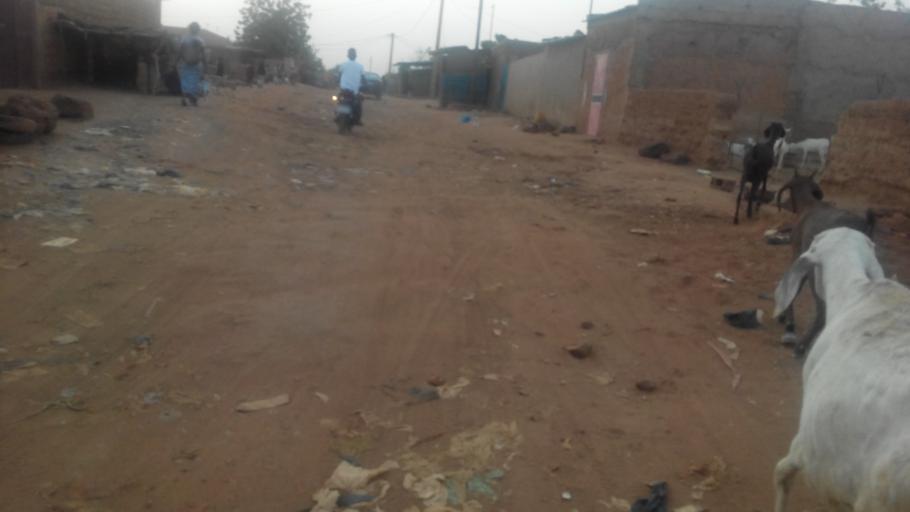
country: NE
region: Niamey
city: Niamey
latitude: 13.5511
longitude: 2.0547
